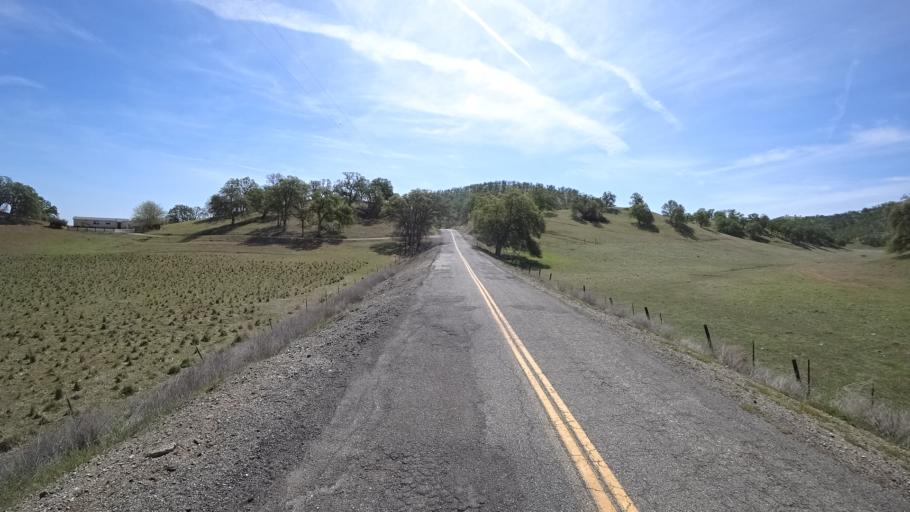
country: US
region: California
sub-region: Glenn County
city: Willows
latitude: 39.5442
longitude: -122.4291
